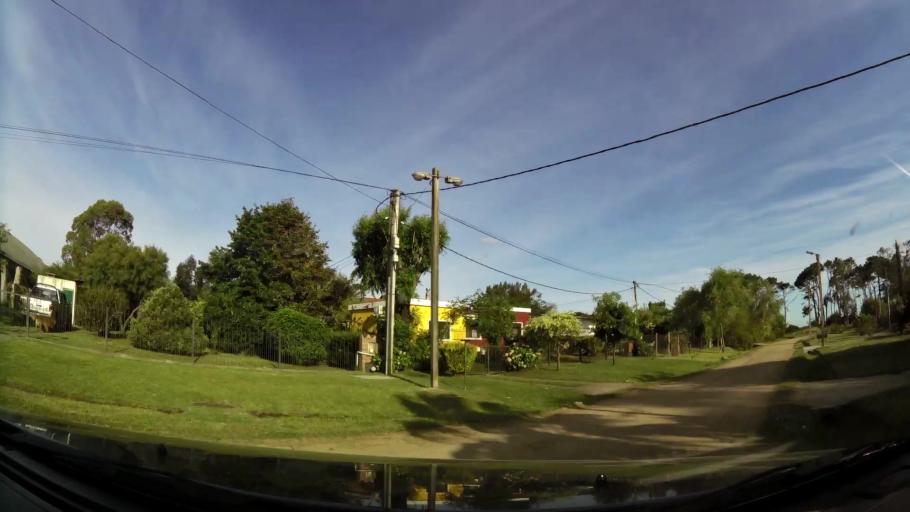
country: UY
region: Canelones
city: Atlantida
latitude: -34.7890
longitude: -55.8533
